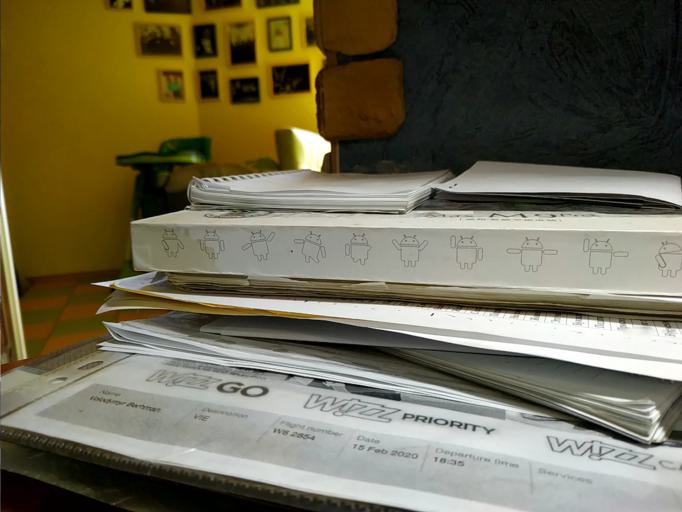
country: RU
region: Pskov
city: Plyussa
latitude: 58.7040
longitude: 29.2700
